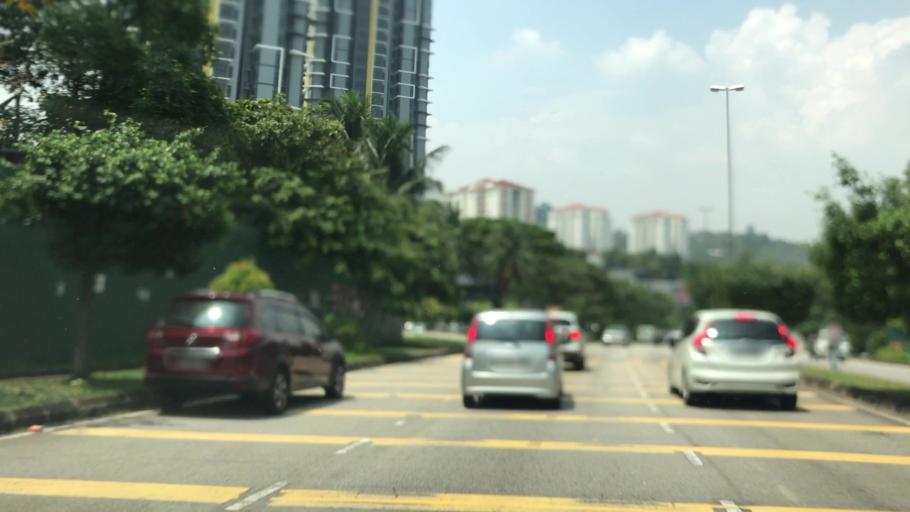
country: MY
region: Selangor
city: Subang Jaya
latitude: 3.0230
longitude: 101.6228
